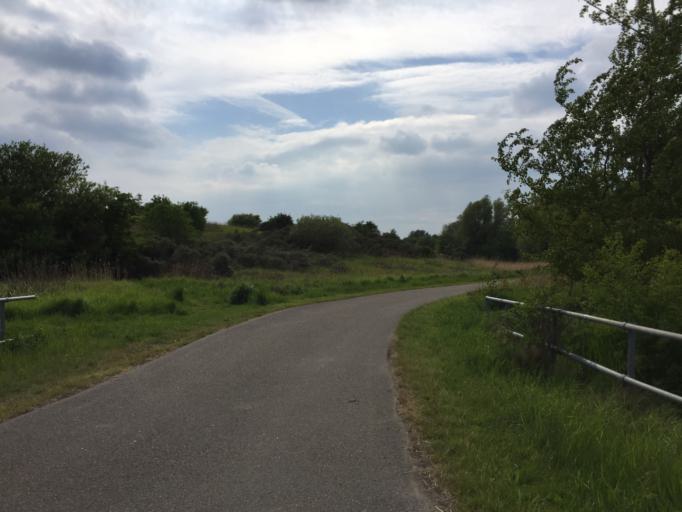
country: DK
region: Capital Region
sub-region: Hvidovre Kommune
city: Hvidovre
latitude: 55.6179
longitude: 12.4658
